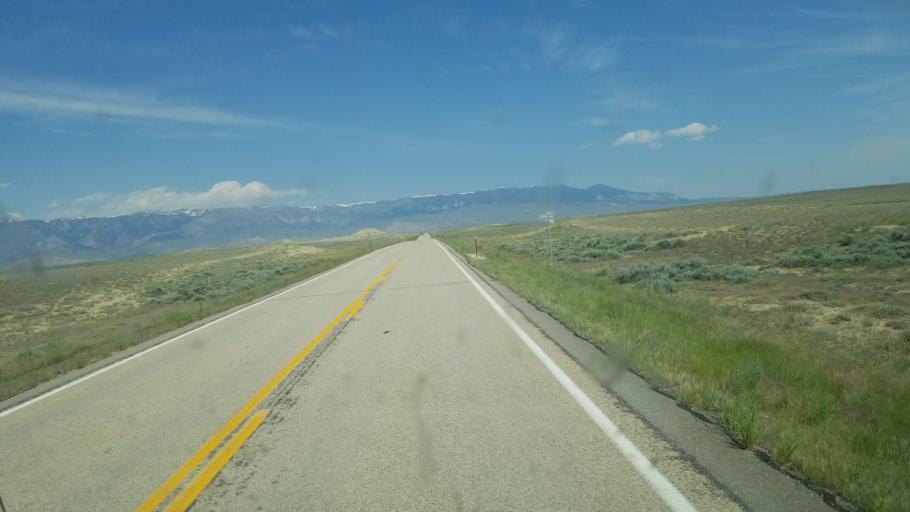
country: US
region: Wyoming
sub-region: Park County
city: Powell
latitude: 44.8741
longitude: -109.0524
